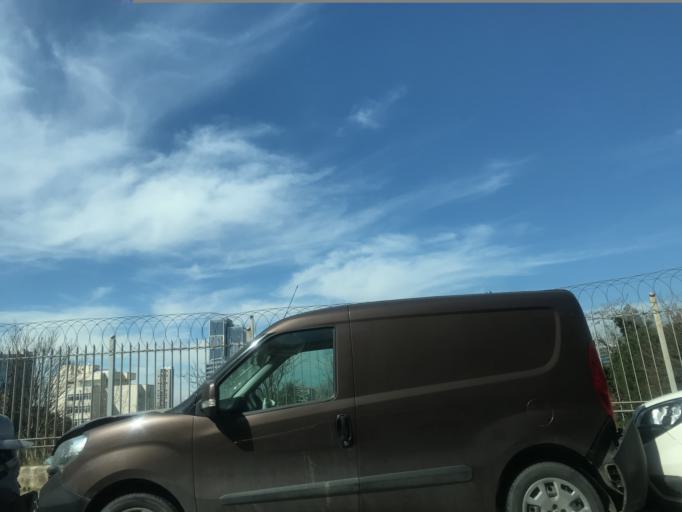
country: TR
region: Istanbul
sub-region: Atasehir
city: Atasehir
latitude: 40.9708
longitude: 29.1082
